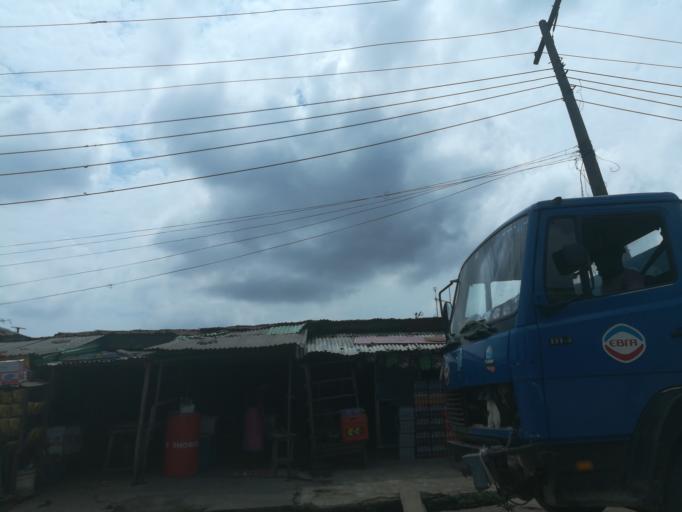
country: NG
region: Lagos
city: Somolu
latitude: 6.5417
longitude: 3.3931
